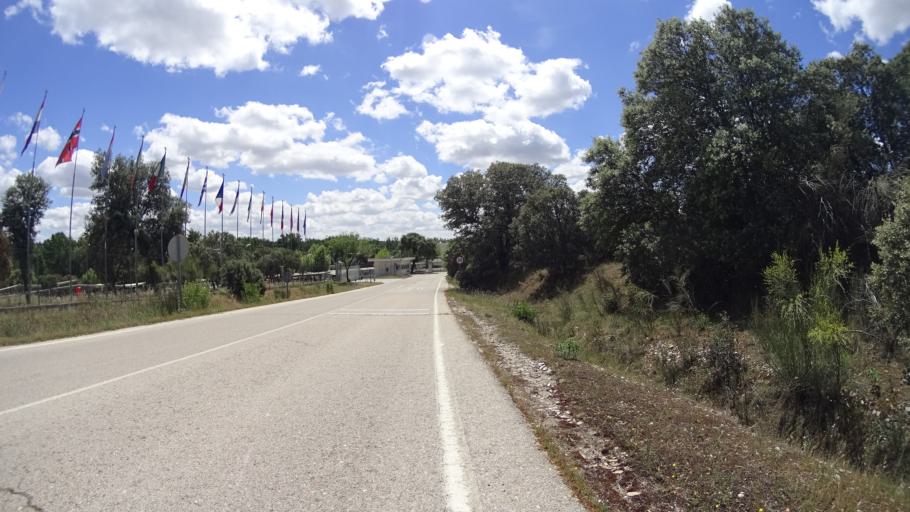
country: ES
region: Madrid
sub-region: Provincia de Madrid
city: Villanueva del Pardillo
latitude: 40.4455
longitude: -3.9530
